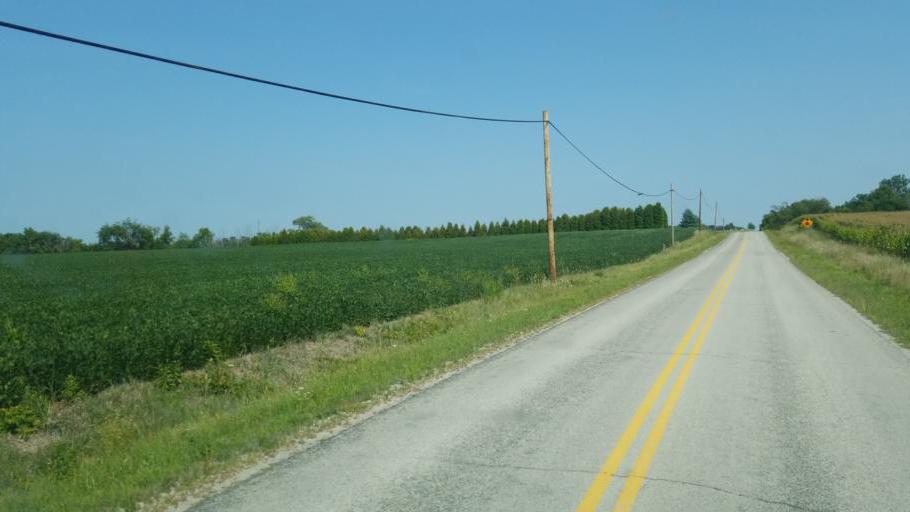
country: US
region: Ohio
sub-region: Crawford County
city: Crestline
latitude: 40.8866
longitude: -82.7759
